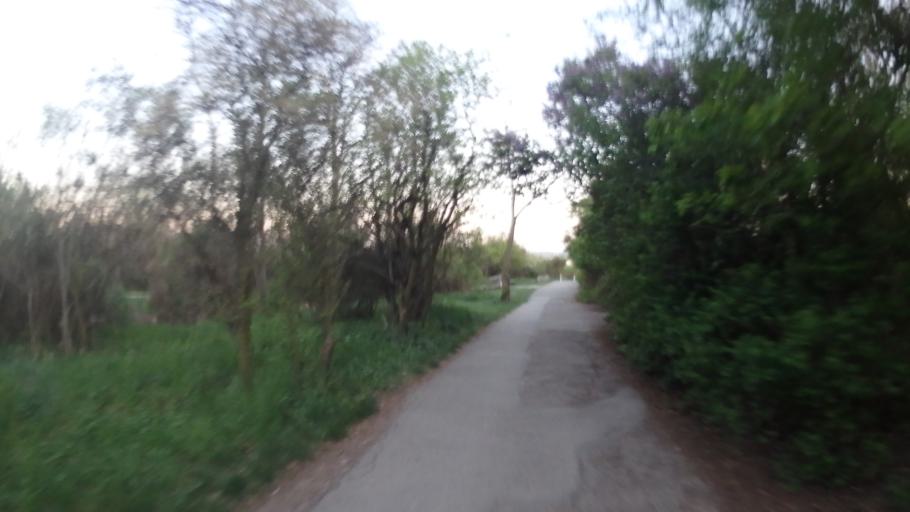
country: CZ
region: South Moravian
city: Ostopovice
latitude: 49.1791
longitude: 16.5557
